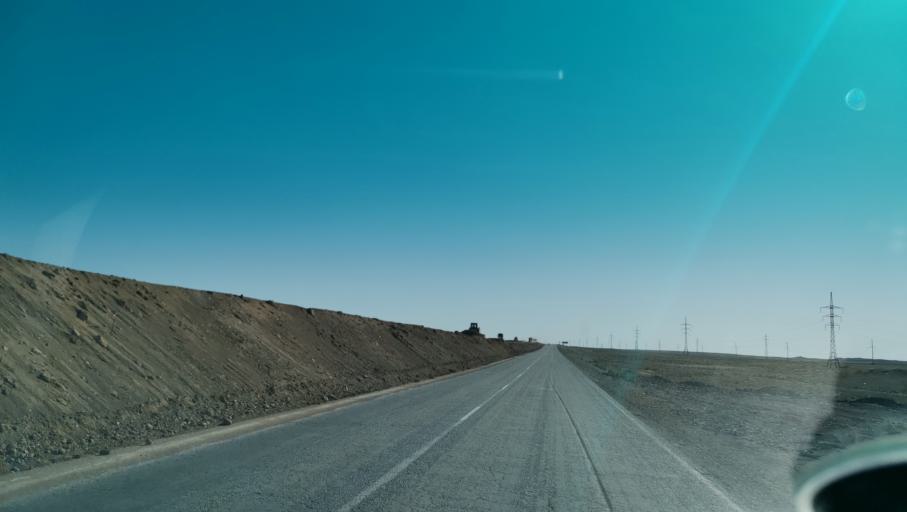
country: KZ
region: Qaraghandy
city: Balqash
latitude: 46.7155
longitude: 74.4683
